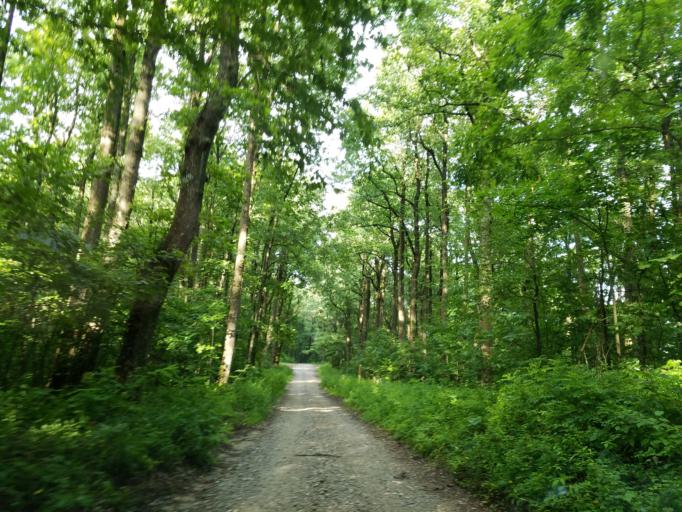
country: US
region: Georgia
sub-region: Lumpkin County
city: Dahlonega
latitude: 34.6522
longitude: -84.1394
